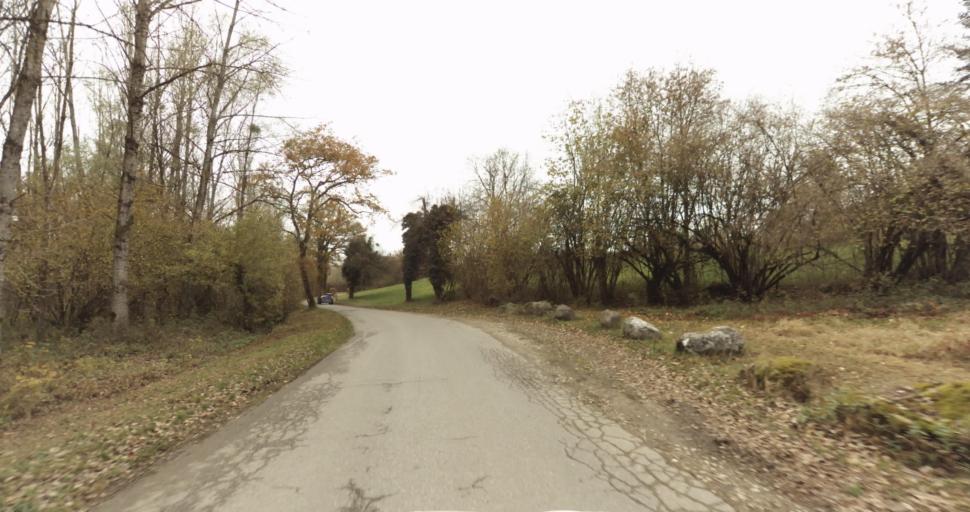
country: FR
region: Rhone-Alpes
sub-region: Departement de la Haute-Savoie
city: Viuz-la-Chiesaz
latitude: 45.8487
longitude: 6.0543
